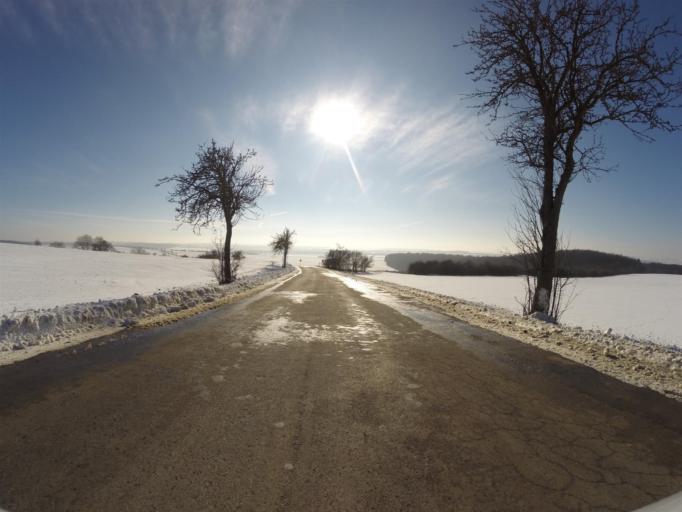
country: DE
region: Thuringia
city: Bucha
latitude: 50.8963
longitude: 11.5066
